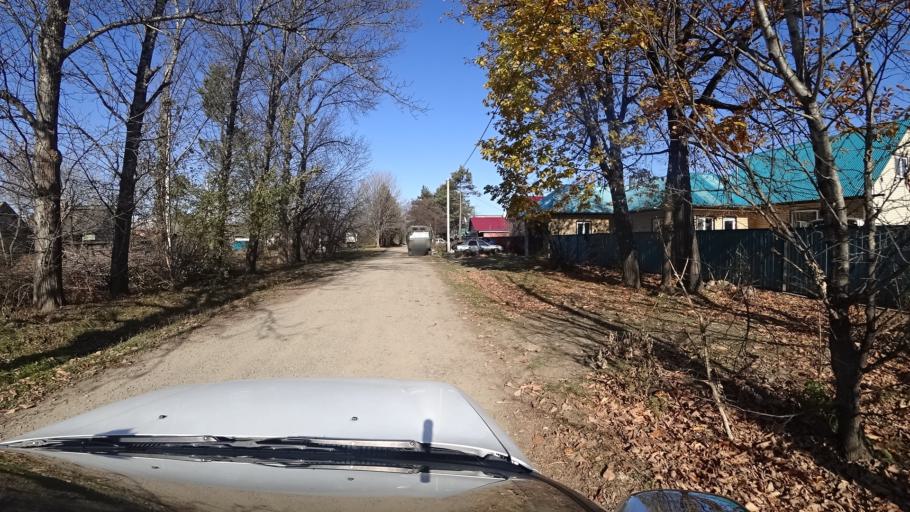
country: RU
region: Primorskiy
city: Dal'nerechensk
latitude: 45.9083
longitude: 133.7997
